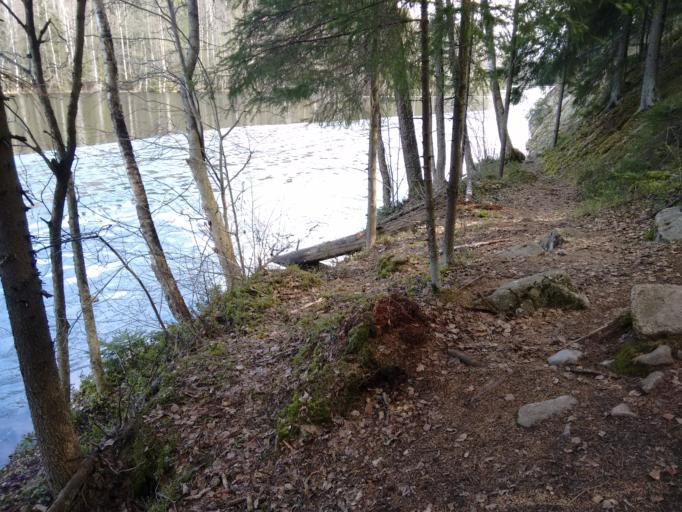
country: FI
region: Pirkanmaa
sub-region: Tampere
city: Tampere
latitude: 61.4436
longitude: 23.8211
